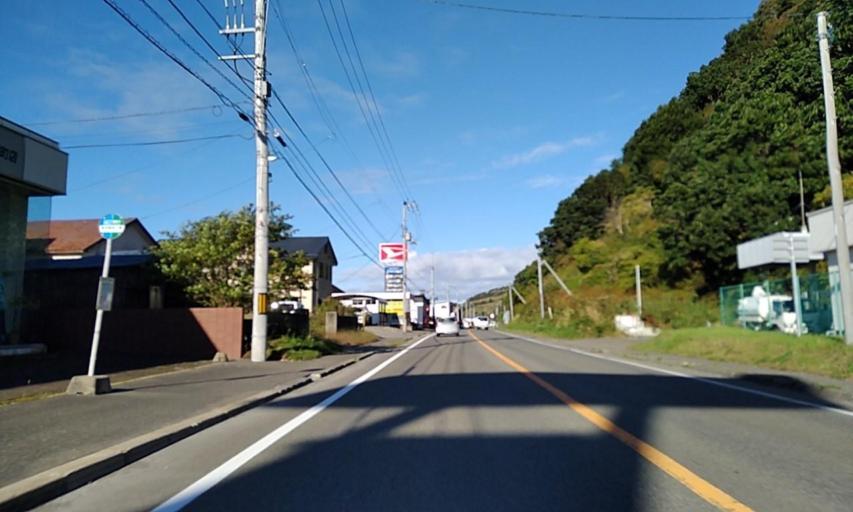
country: JP
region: Hokkaido
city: Shizunai-furukawacho
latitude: 42.1767
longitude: 142.7551
